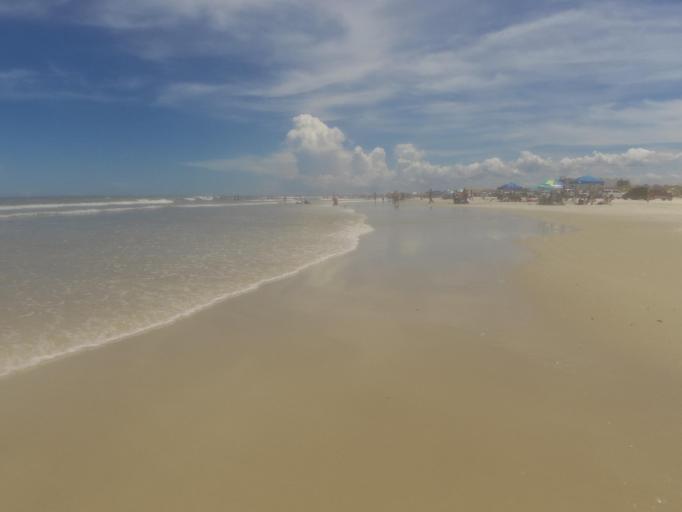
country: US
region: Florida
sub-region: Saint Johns County
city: Butler Beach
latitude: 29.8215
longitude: -81.2621
